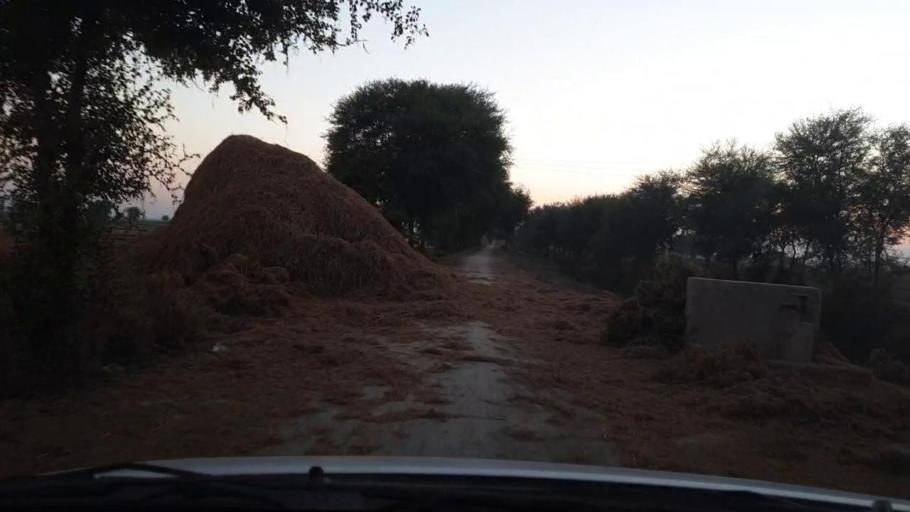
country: PK
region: Sindh
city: Khairpur Nathan Shah
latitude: 27.1512
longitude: 67.6912
